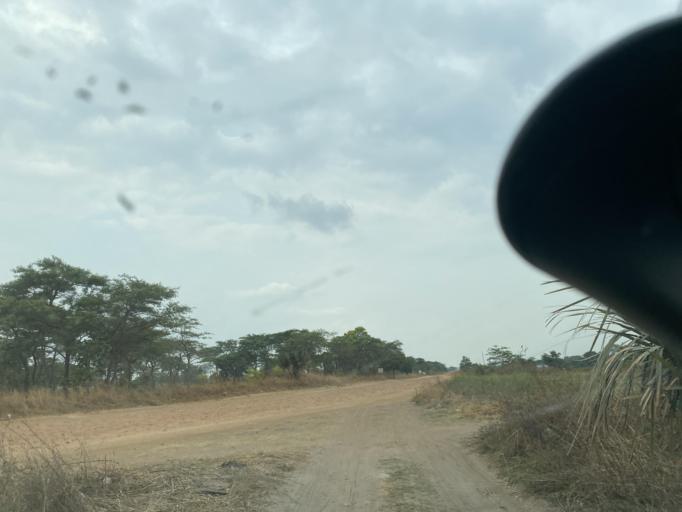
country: ZM
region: Lusaka
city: Lusaka
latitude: -15.2310
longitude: 28.3354
